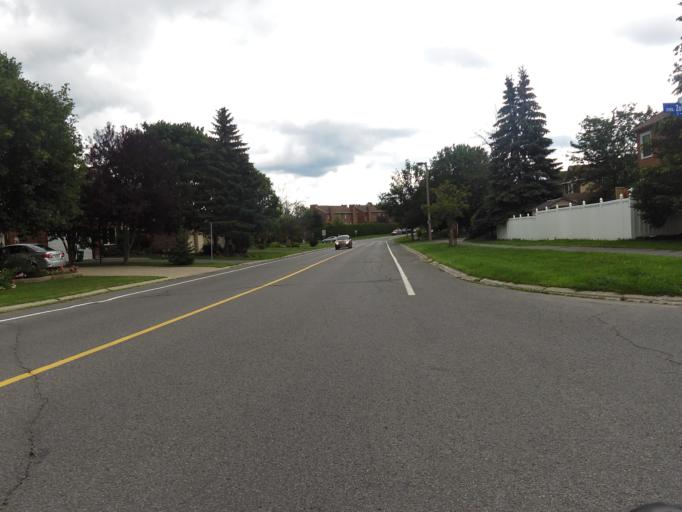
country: CA
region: Ontario
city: Bells Corners
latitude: 45.3271
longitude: -75.9129
